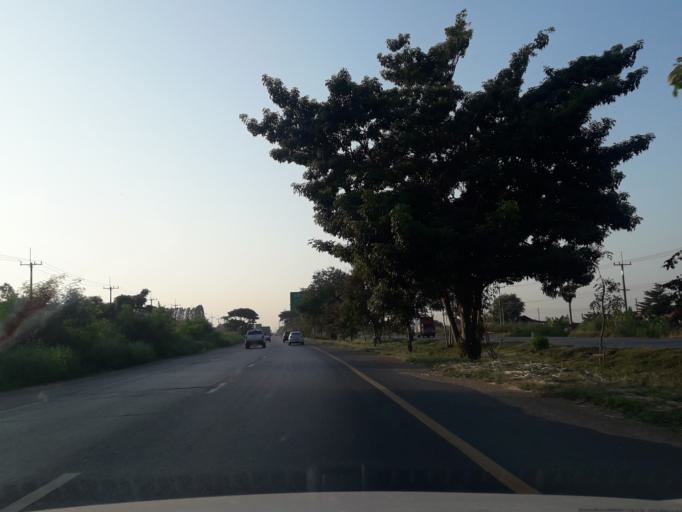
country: TH
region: Phra Nakhon Si Ayutthaya
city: Bang Pa-in
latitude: 14.2213
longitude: 100.5416
